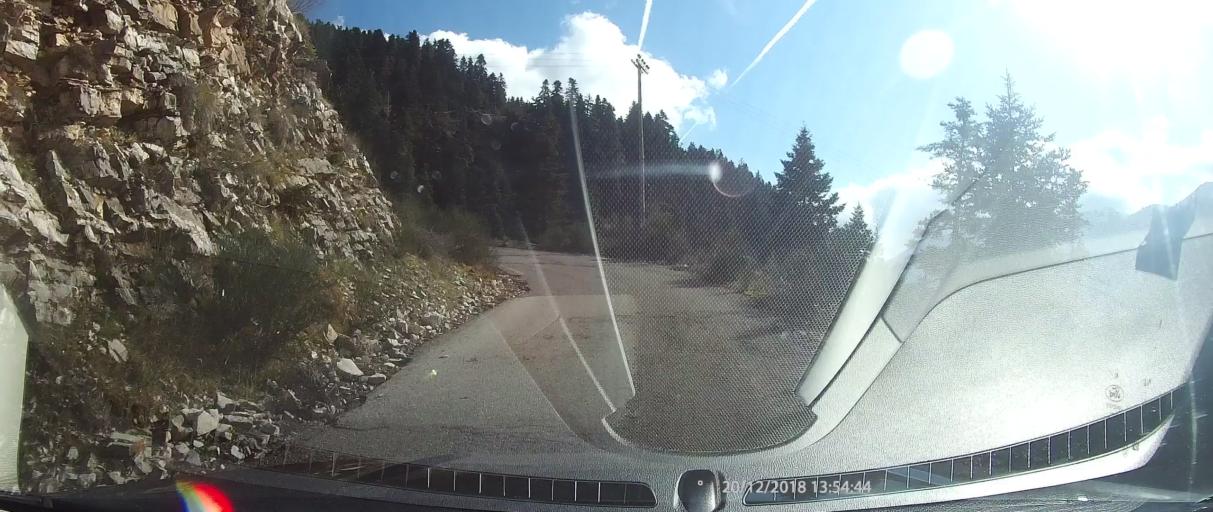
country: GR
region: West Greece
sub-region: Nomos Aitolias kai Akarnanias
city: Paravola
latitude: 38.7136
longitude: 21.6118
